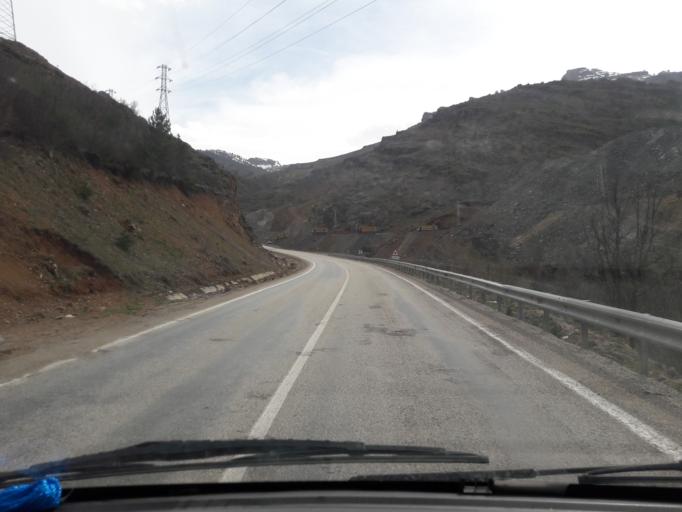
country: TR
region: Gumushane
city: Gumushkhane
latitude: 40.3035
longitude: 39.4755
